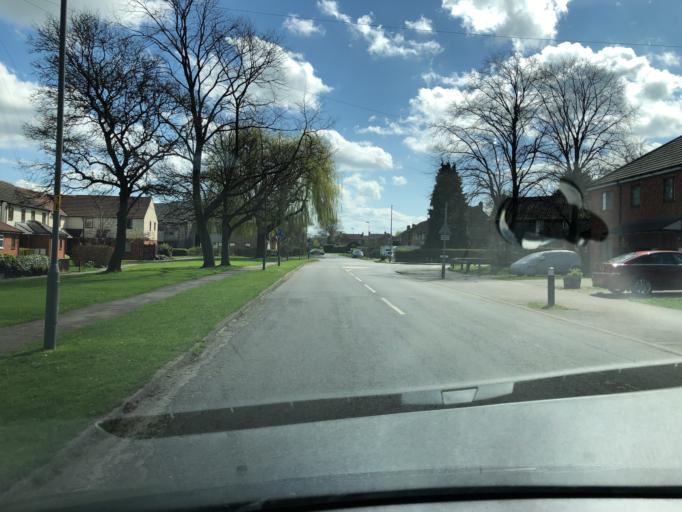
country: GB
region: England
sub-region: North Yorkshire
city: Northallerton
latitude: 54.3376
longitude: -1.4247
